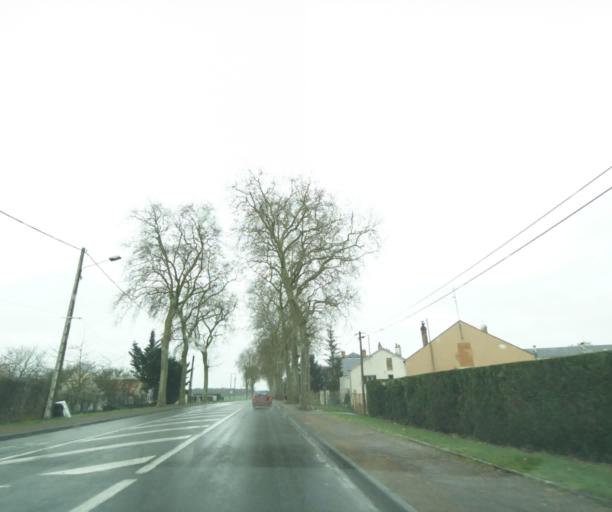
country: FR
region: Centre
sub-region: Departement du Loiret
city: Chevilly
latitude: 48.0222
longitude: 1.8753
